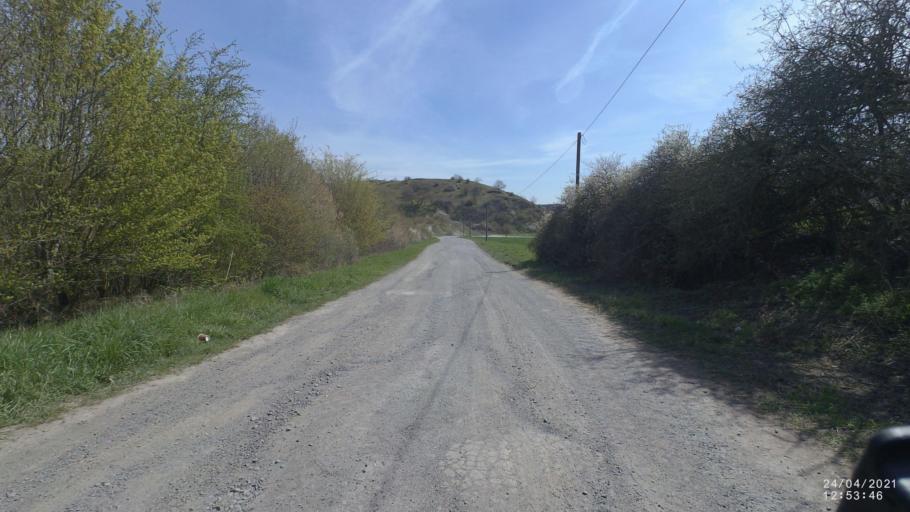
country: DE
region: Rheinland-Pfalz
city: Thur
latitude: 50.3277
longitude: 7.2778
